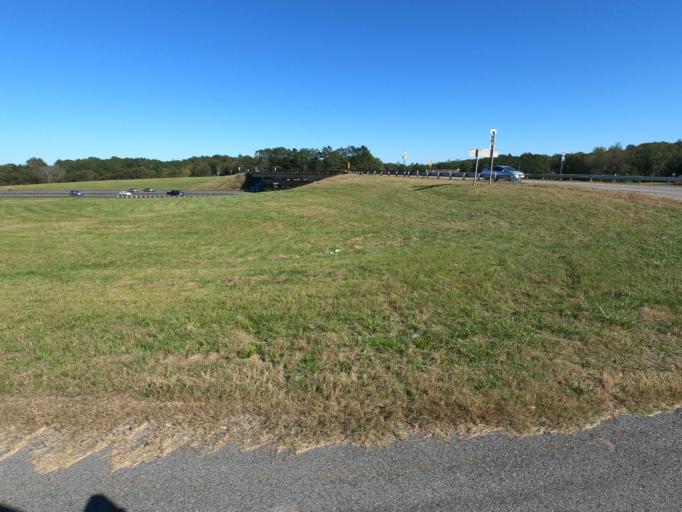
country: US
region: Alabama
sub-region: Limestone County
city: Ardmore
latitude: 34.9728
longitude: -86.8844
